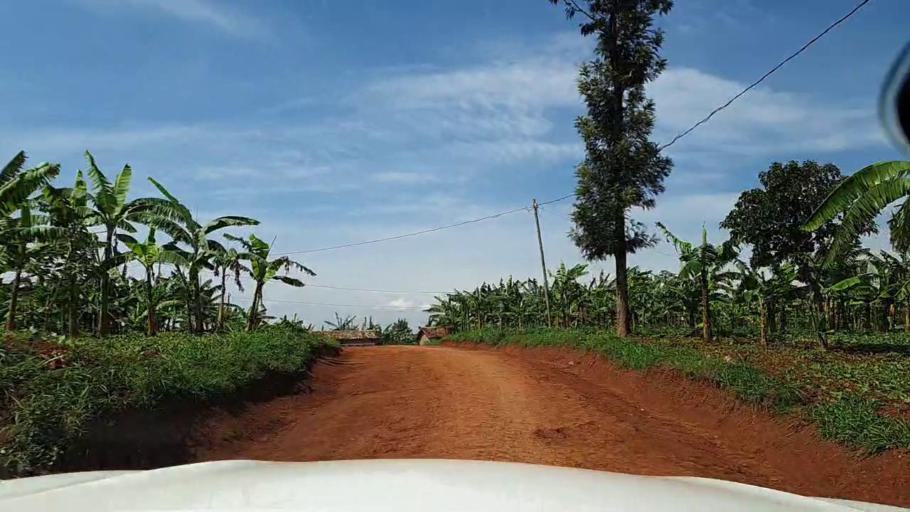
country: RW
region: Southern Province
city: Butare
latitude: -2.7022
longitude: 29.8487
